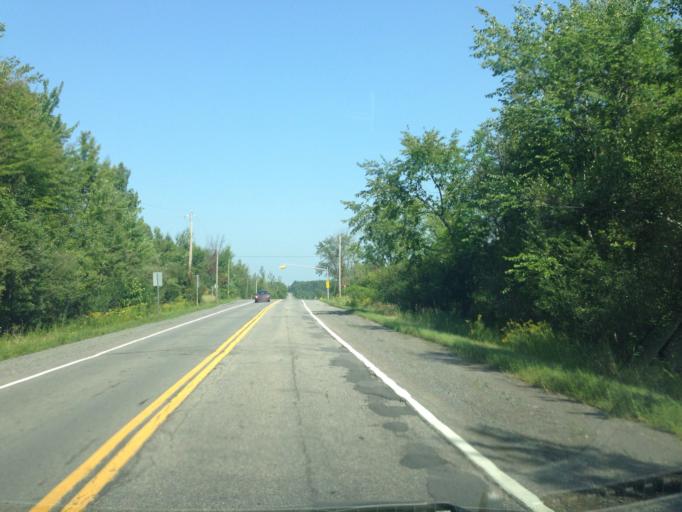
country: CA
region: Ontario
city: Ottawa
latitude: 45.3915
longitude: -75.5513
